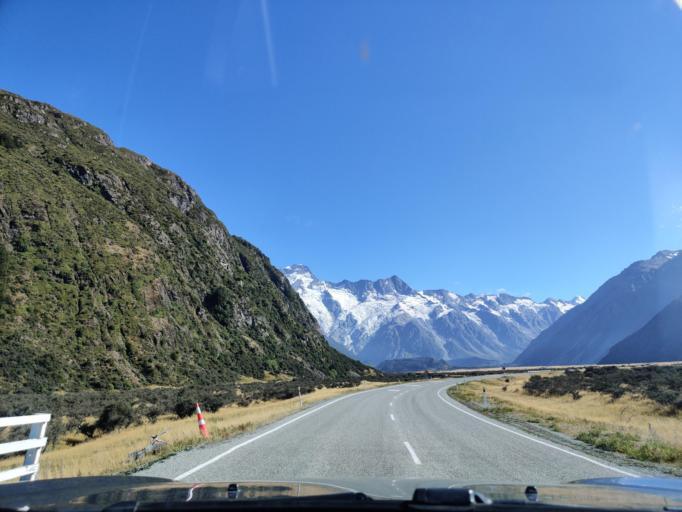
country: NZ
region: Canterbury
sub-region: Timaru District
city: Pleasant Point
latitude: -43.7574
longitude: 170.1179
